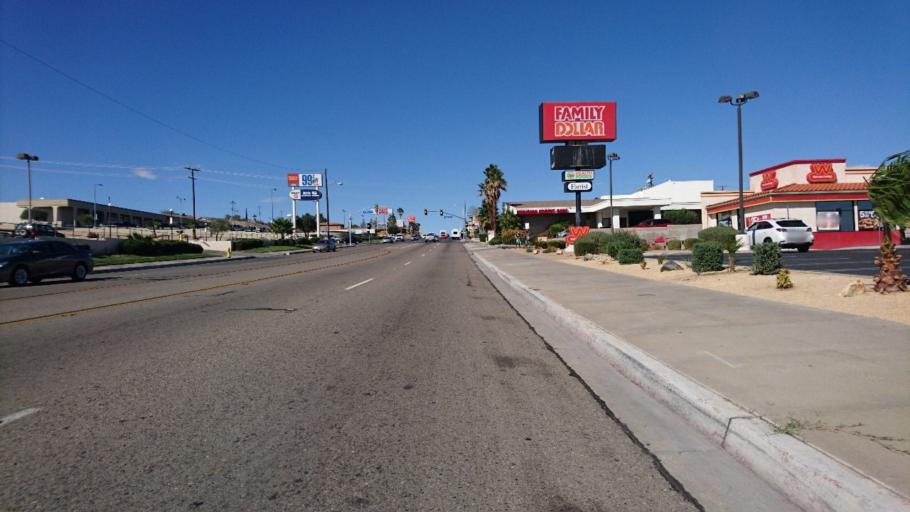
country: US
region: California
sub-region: San Bernardino County
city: Barstow
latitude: 34.8956
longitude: -117.0062
